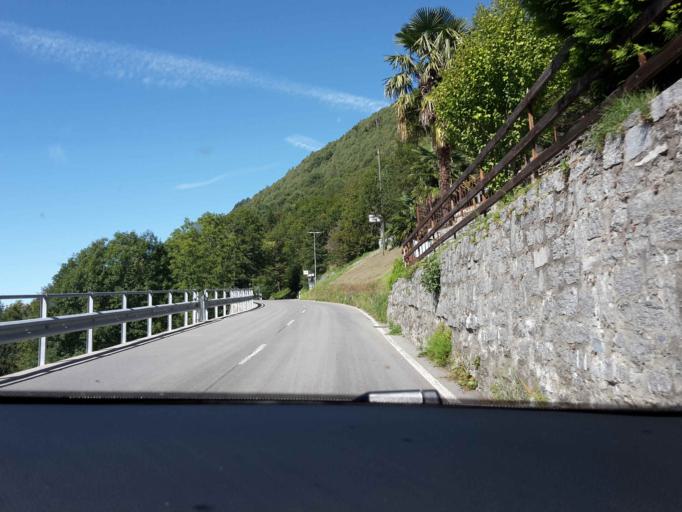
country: CH
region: Ticino
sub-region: Bellinzona District
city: Bellinzona
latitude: 46.1689
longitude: 9.0536
